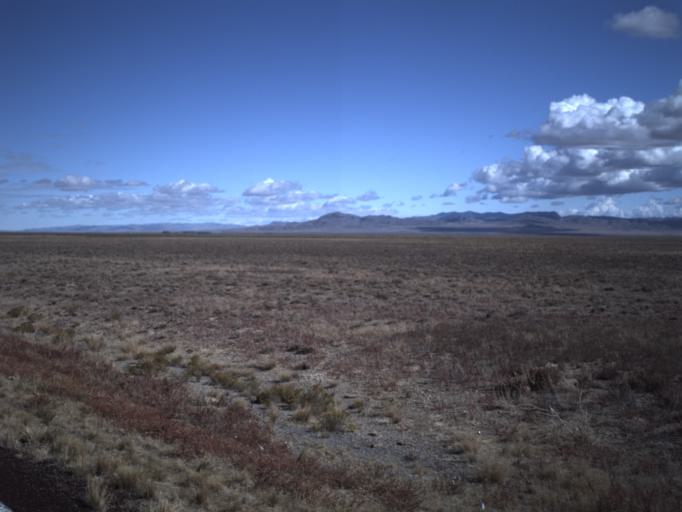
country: US
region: Nevada
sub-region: White Pine County
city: McGill
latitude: 38.9783
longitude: -114.0341
